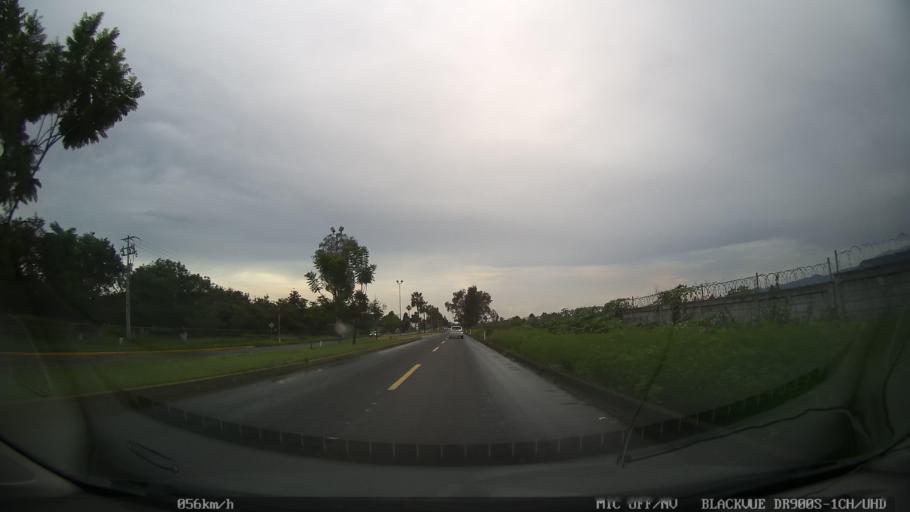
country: MX
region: Michoacan
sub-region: Uruapan
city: Santa Rosa (Santa Barbara)
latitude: 19.3875
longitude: -102.0417
